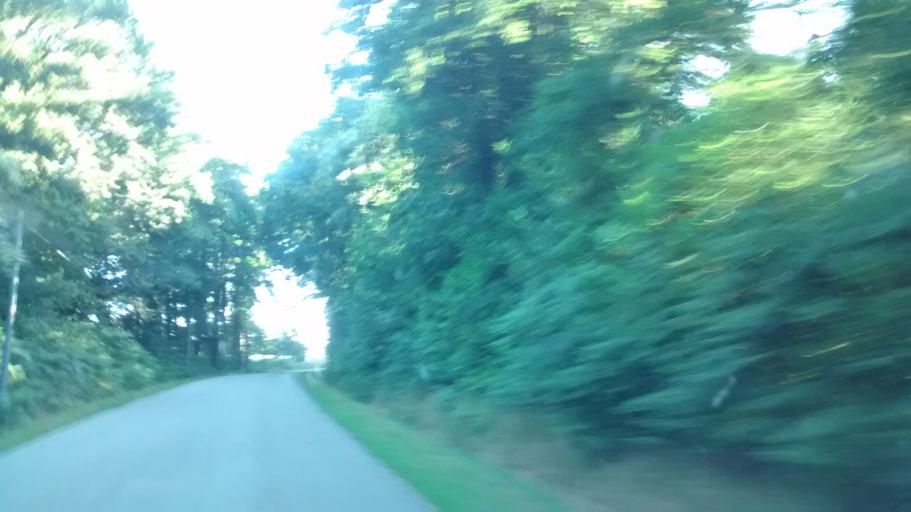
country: FR
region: Brittany
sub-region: Departement du Morbihan
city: Campeneac
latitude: 47.9809
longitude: -2.3097
